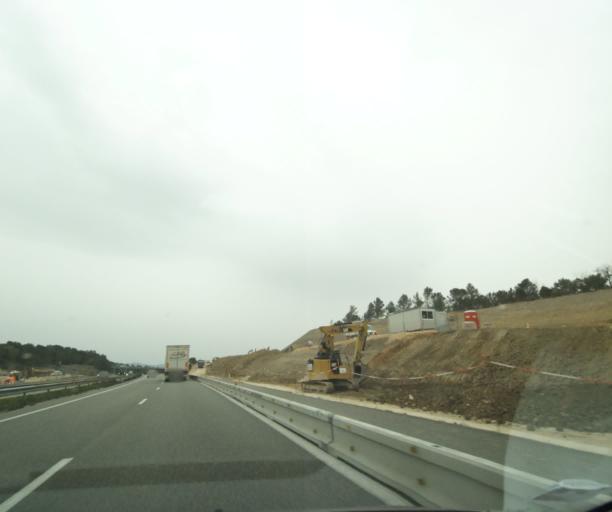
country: FR
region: Provence-Alpes-Cote d'Azur
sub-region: Departement des Bouches-du-Rhone
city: Belcodene
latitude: 43.4187
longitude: 5.5757
